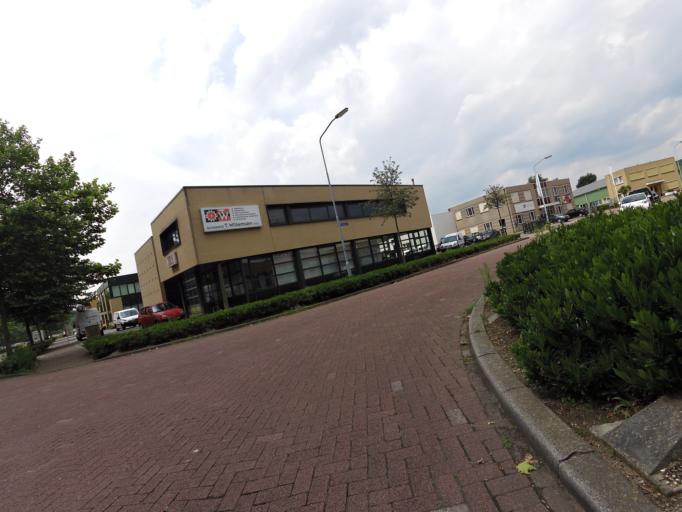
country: NL
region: Gelderland
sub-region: Gemeente Zevenaar
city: Zevenaar
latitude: 51.9310
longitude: 6.1157
